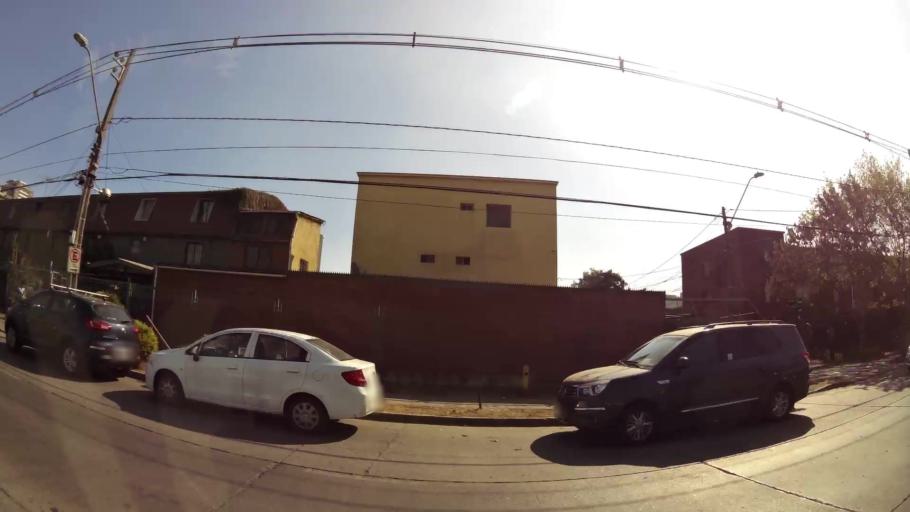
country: CL
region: Santiago Metropolitan
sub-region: Provincia de Santiago
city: Santiago
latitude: -33.4689
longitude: -70.6231
